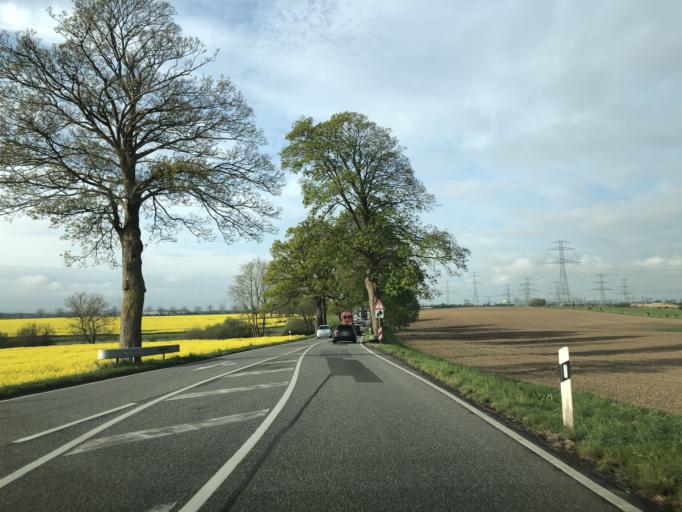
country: DE
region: Mecklenburg-Vorpommern
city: Guestrow
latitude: 53.8250
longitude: 12.2026
